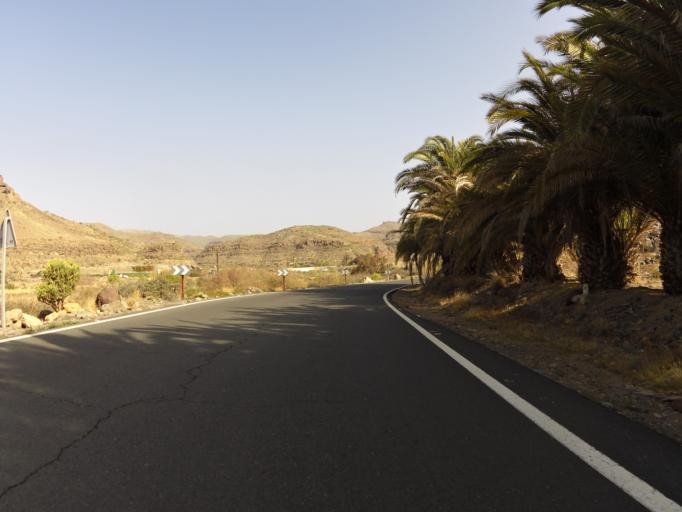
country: ES
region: Canary Islands
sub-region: Provincia de Las Palmas
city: Puerto Rico
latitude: 27.7754
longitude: -15.6666
